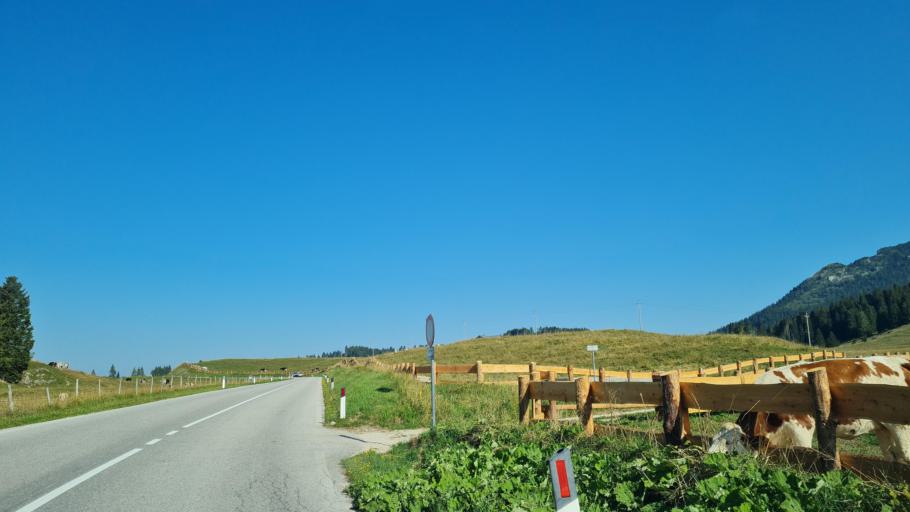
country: IT
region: Trentino-Alto Adige
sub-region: Provincia di Trento
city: Luserna
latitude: 45.9536
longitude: 11.3411
